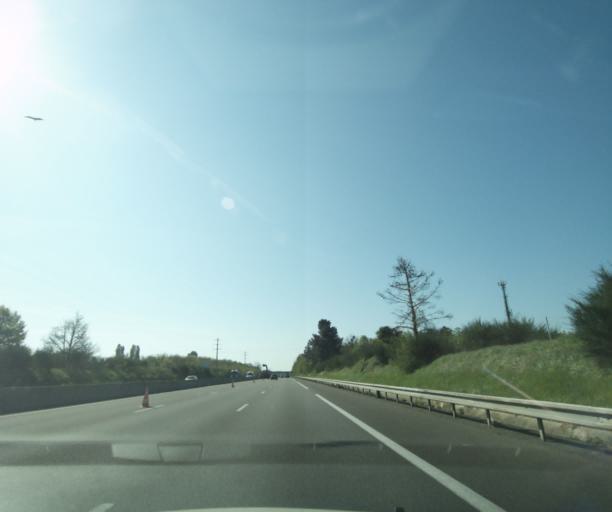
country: FR
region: Centre
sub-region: Departement du Loiret
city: Saint-Pryve-Saint-Mesmin
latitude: 47.8610
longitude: 1.8642
